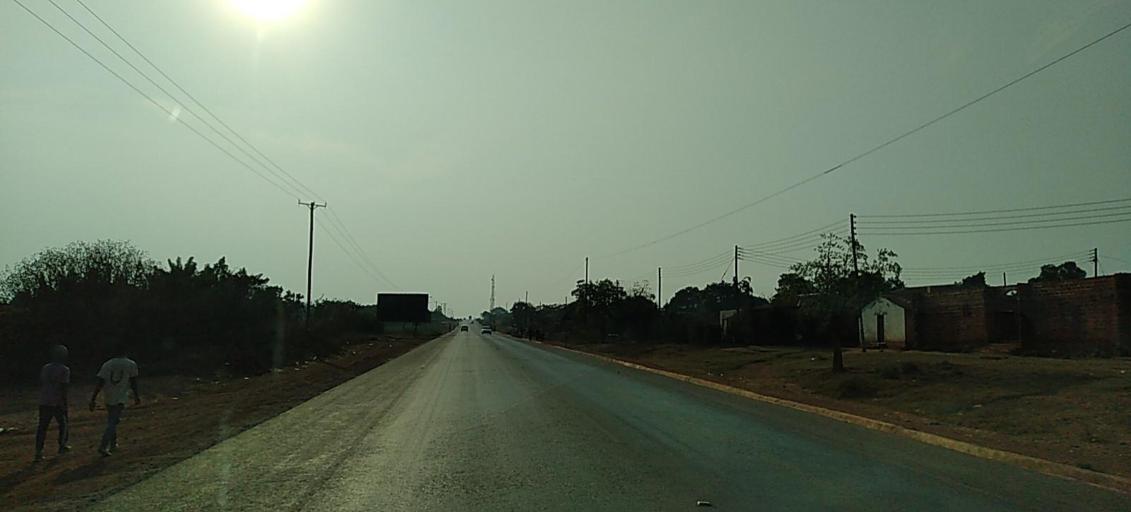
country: ZM
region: North-Western
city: Solwezi
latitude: -12.1898
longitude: 26.4355
